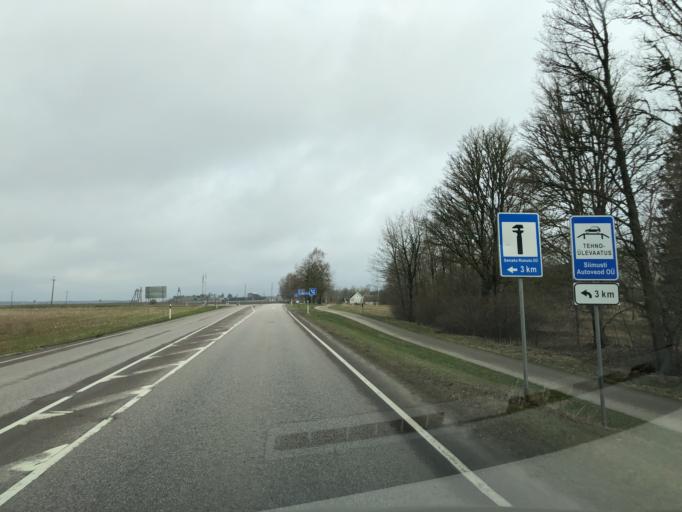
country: EE
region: Jogevamaa
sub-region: Jogeva linn
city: Jogeva
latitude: 58.7289
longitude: 26.3849
